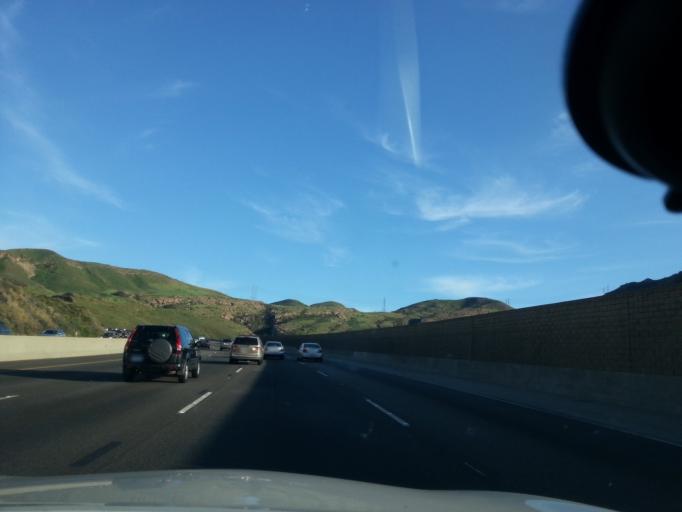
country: US
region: California
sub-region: Ventura County
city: Casa Conejo
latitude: 34.2029
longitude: -118.9803
